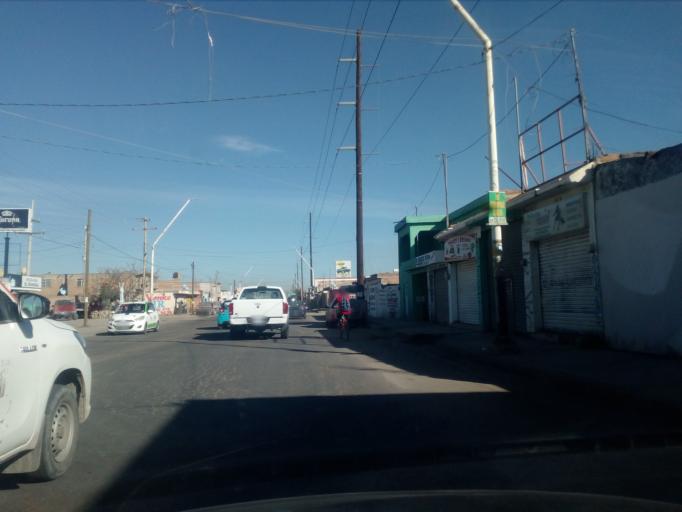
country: MX
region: Durango
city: Victoria de Durango
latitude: 24.0147
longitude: -104.6326
